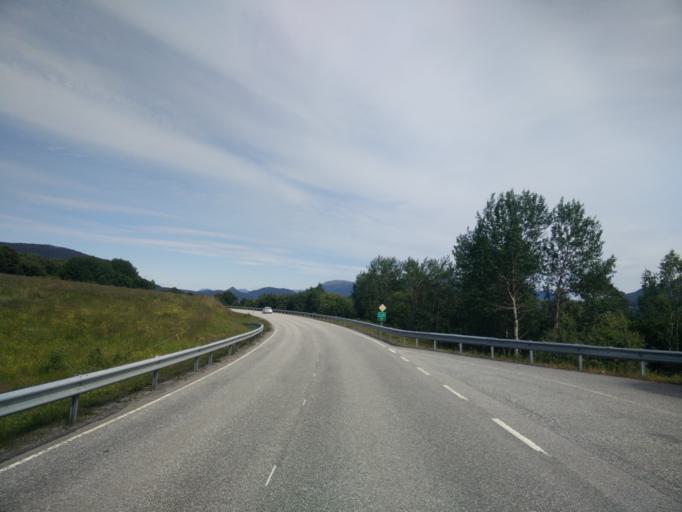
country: NO
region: More og Romsdal
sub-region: Kristiansund
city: Rensvik
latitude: 62.9763
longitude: 7.8586
